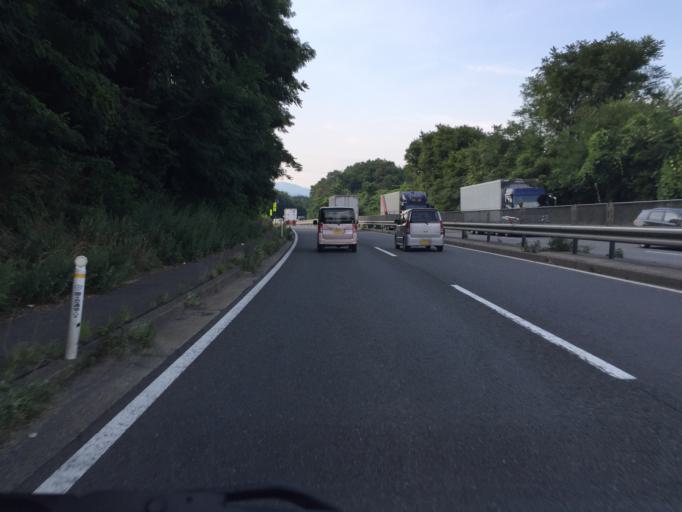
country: JP
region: Fukushima
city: Fukushima-shi
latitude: 37.7047
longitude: 140.4631
